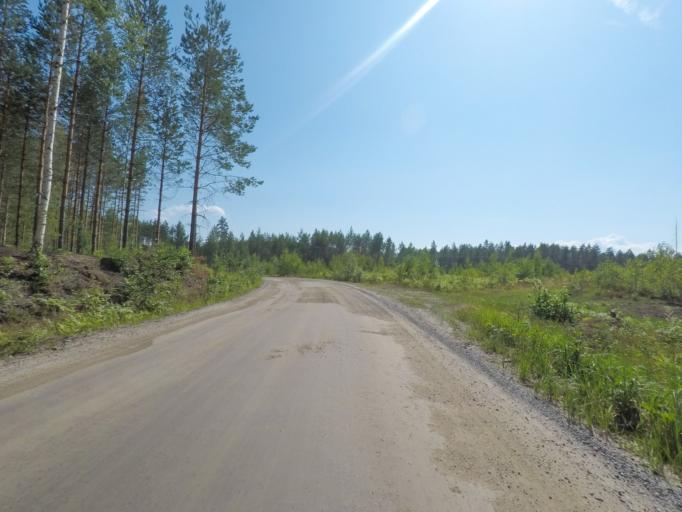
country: FI
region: Southern Savonia
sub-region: Mikkeli
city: Puumala
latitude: 61.4067
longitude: 28.0462
